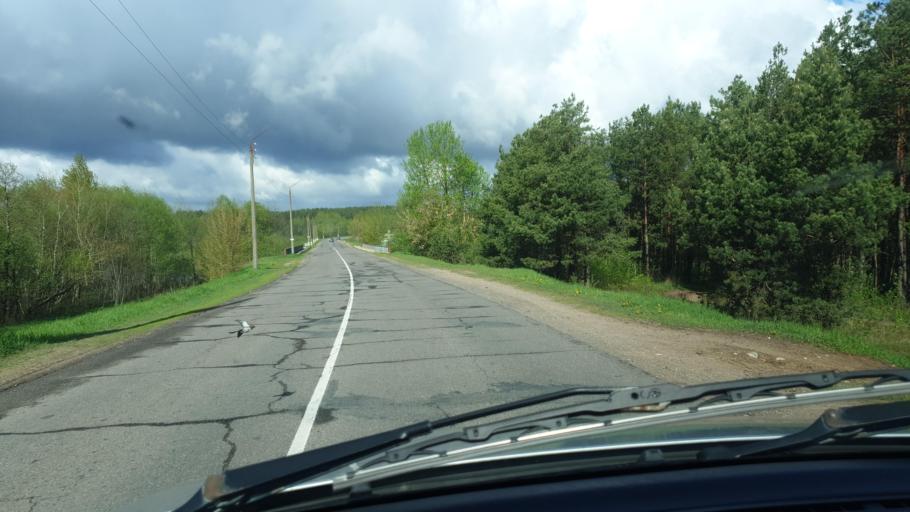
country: BY
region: Vitebsk
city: Lyepyel'
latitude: 54.8767
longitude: 28.6702
